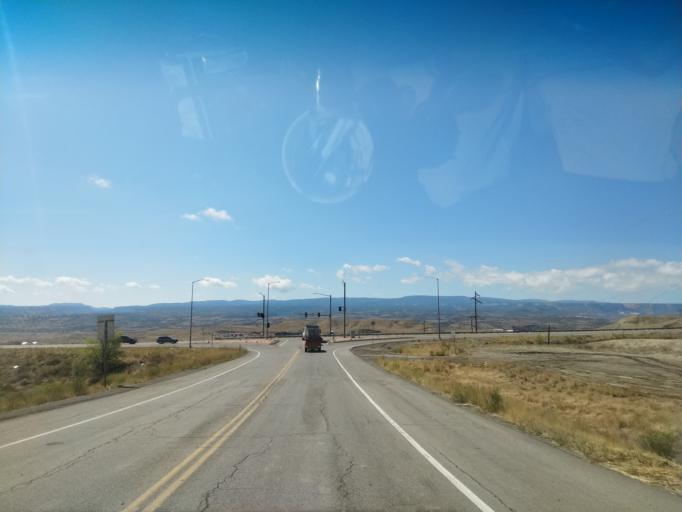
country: US
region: Colorado
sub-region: Mesa County
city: Fruitvale
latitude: 39.0153
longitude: -108.4740
